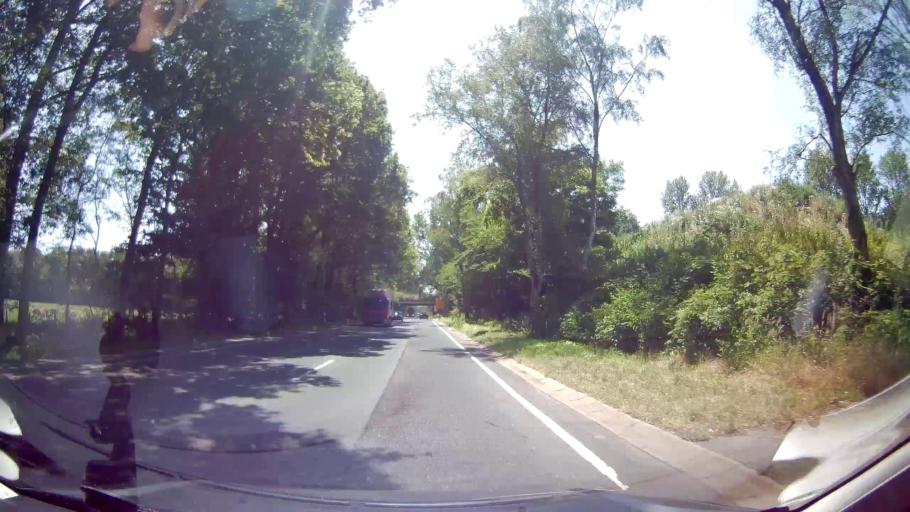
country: DE
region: North Rhine-Westphalia
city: Marl
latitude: 51.6509
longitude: 7.0404
